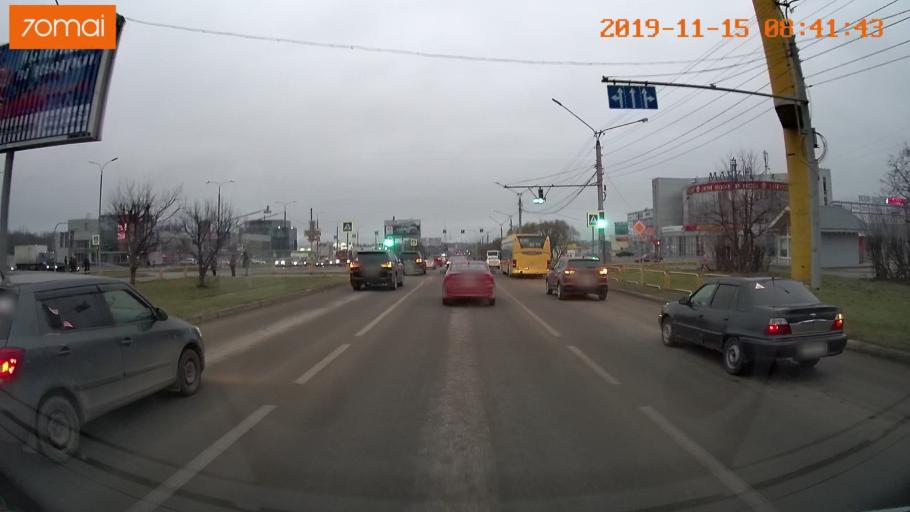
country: RU
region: Vologda
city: Cherepovets
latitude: 59.0979
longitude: 37.9115
